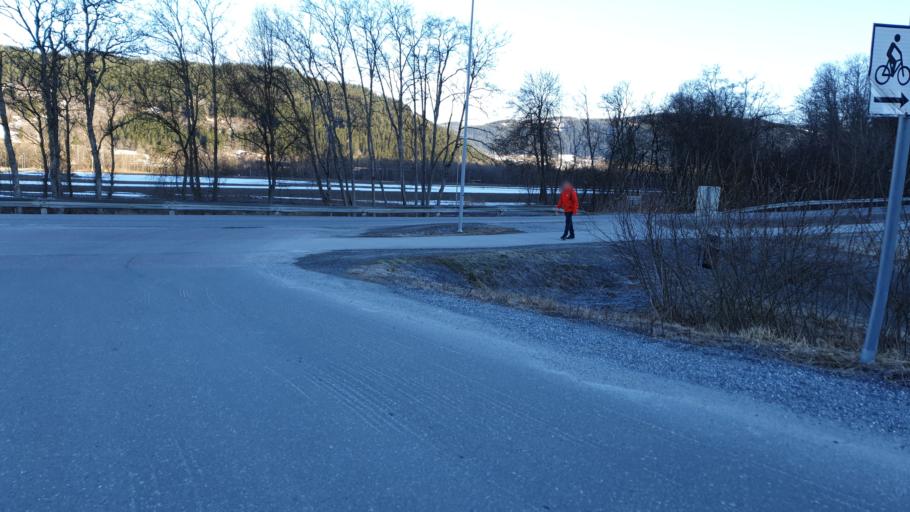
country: NO
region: Sor-Trondelag
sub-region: Orkdal
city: Orkanger
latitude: 63.2904
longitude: 9.8435
